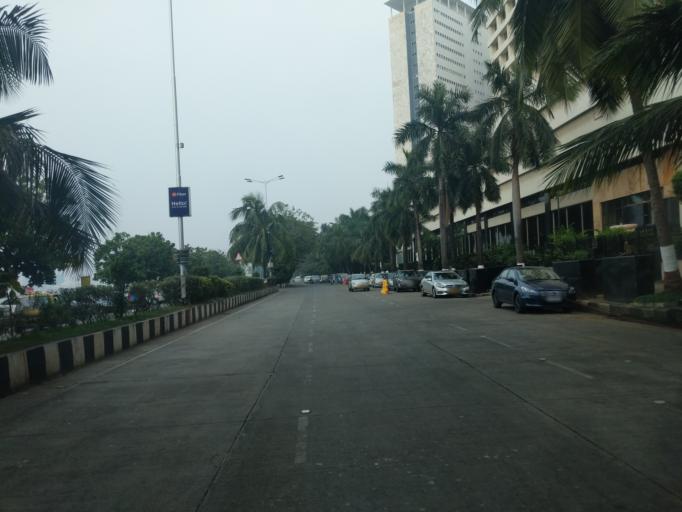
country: IN
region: Maharashtra
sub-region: Raigarh
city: Uran
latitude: 18.9274
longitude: 72.8203
